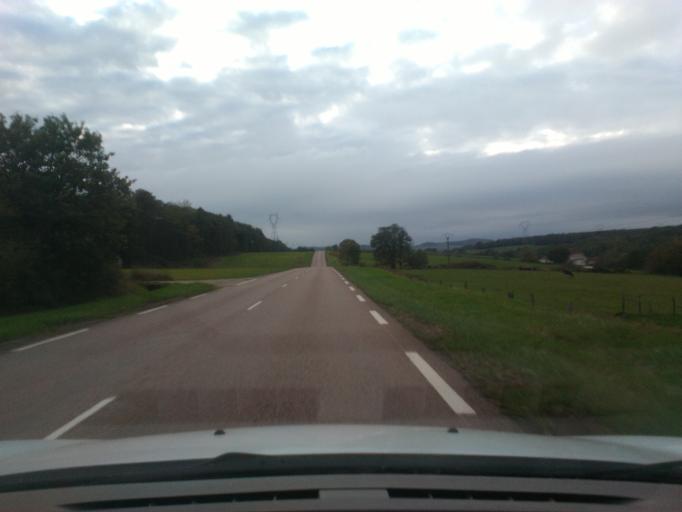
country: FR
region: Lorraine
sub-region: Departement des Vosges
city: Portieux
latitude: 48.3471
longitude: 6.3790
